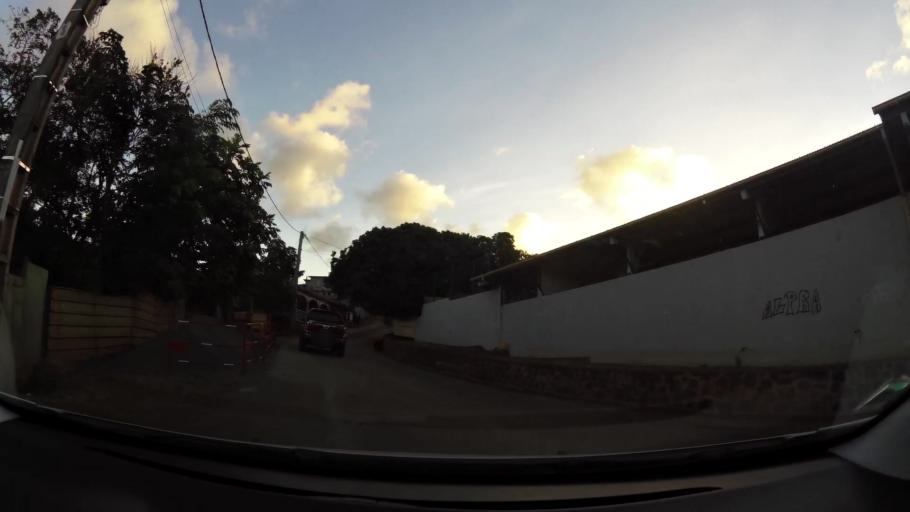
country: YT
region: Dembeni
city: Dembeni
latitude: -12.8666
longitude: 45.1973
